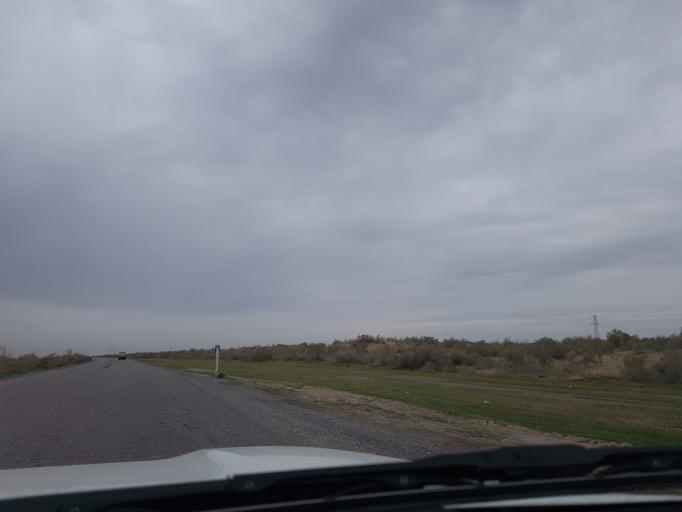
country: TM
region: Lebap
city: Turkmenabat
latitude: 38.8556
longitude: 63.4078
